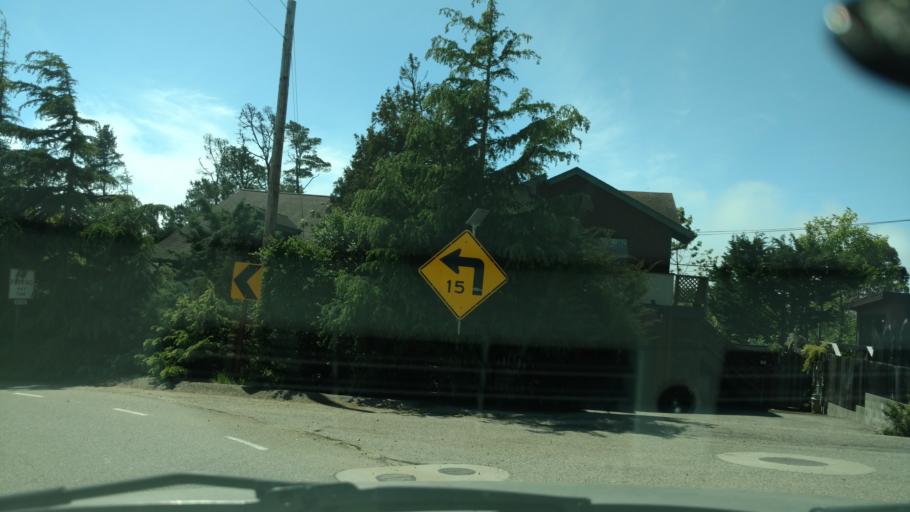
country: US
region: California
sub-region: San Luis Obispo County
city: Cambria
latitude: 35.5569
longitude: -121.0829
